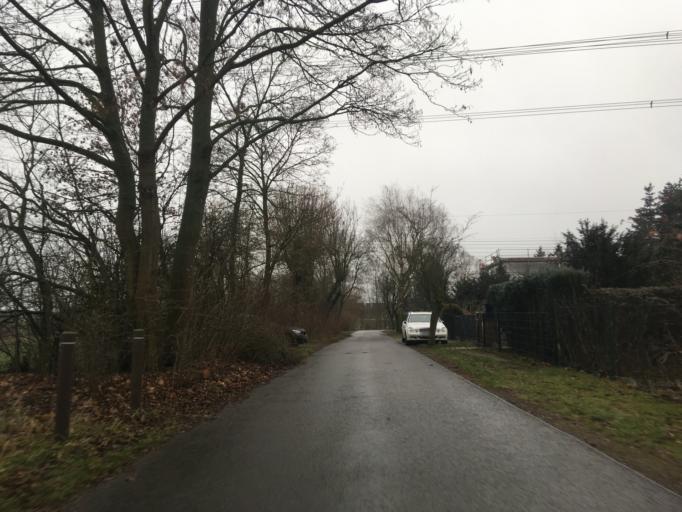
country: DE
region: Berlin
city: Buch
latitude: 52.6217
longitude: 13.5064
